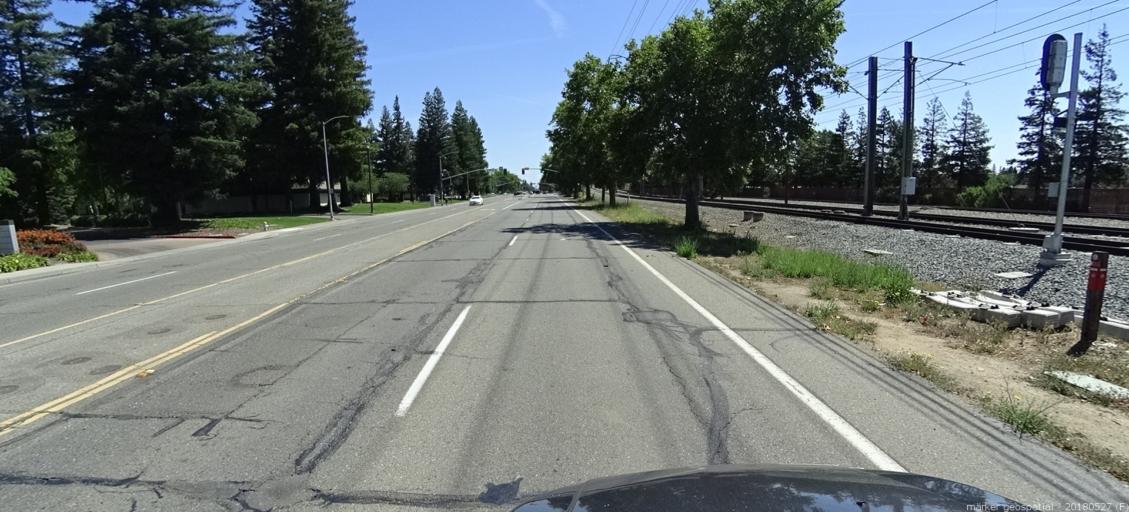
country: US
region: California
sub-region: Sacramento County
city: Rosemont
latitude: 38.5515
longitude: -121.3782
